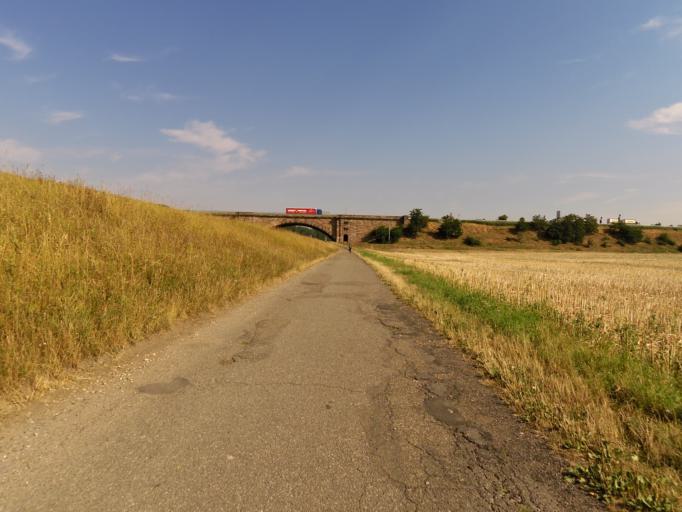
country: DE
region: Hesse
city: Lampertheim
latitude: 49.5486
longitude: 8.4242
